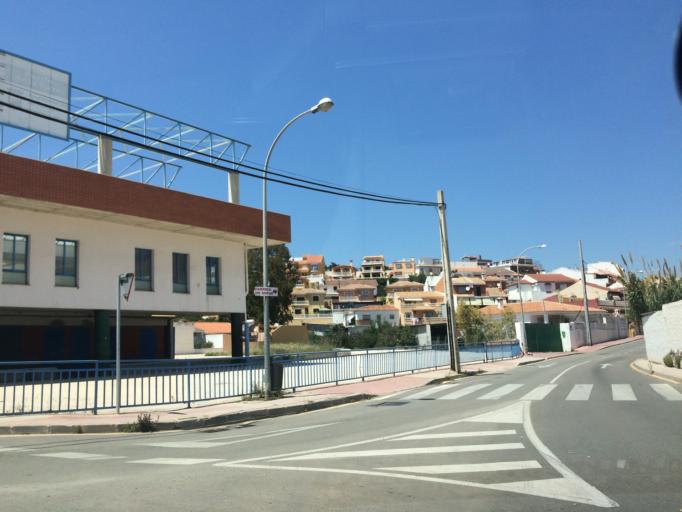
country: ES
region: Andalusia
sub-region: Provincia de Malaga
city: Malaga
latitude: 36.7413
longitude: -4.4826
